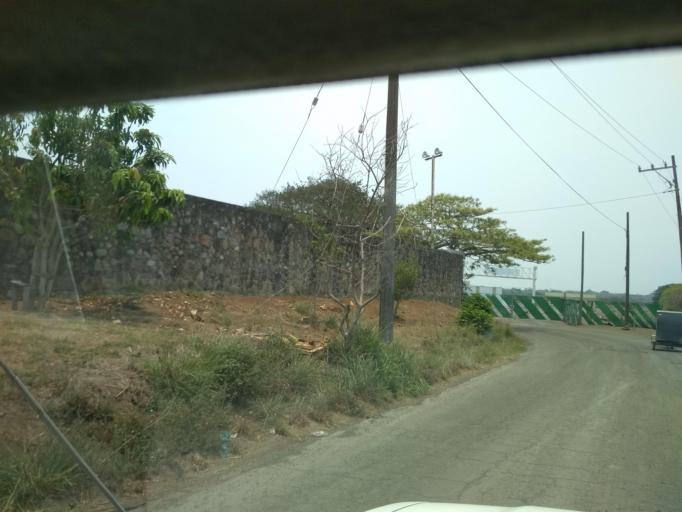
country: MX
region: Veracruz
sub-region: Veracruz
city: Delfino Victoria (Santa Fe)
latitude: 19.2007
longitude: -96.2653
